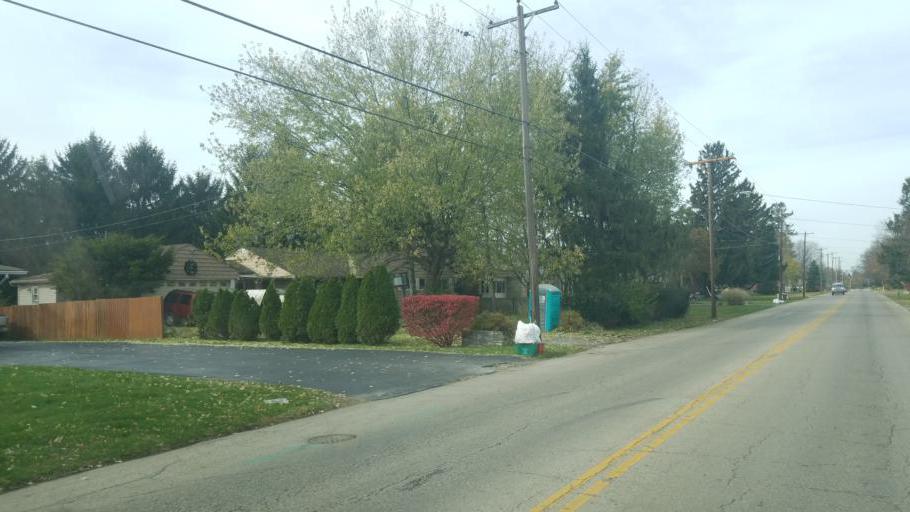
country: US
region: Ohio
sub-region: Madison County
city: London
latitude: 39.8930
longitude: -83.4563
